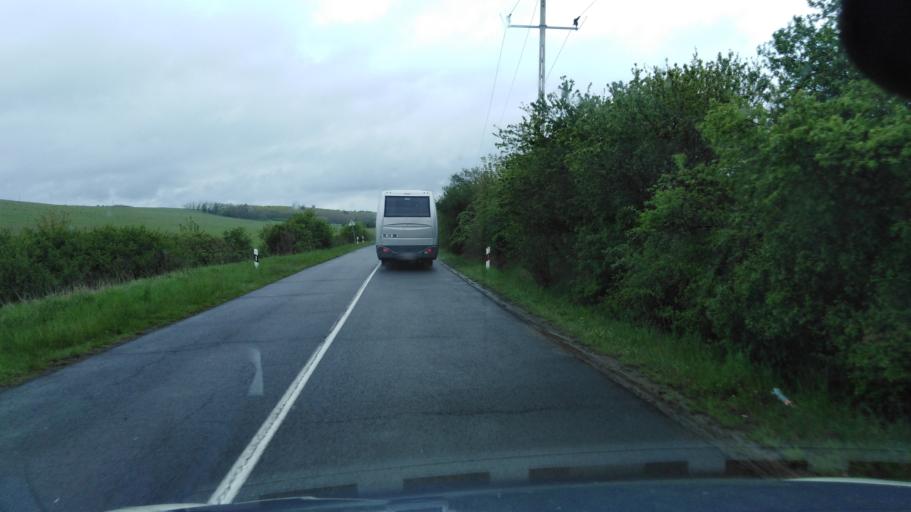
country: HU
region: Nograd
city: Rimoc
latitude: 48.0073
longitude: 19.6087
